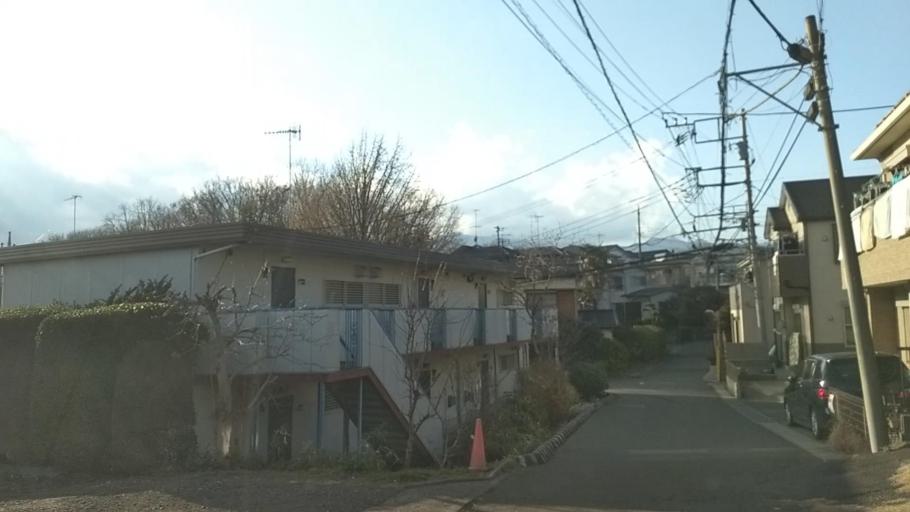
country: JP
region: Kanagawa
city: Atsugi
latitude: 35.4471
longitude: 139.3365
